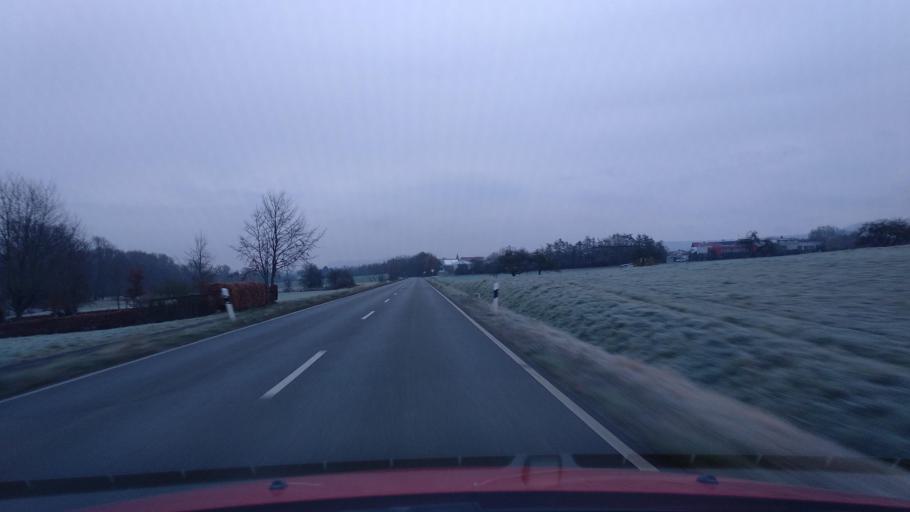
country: DE
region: Hesse
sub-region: Regierungsbezirk Kassel
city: Calden
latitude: 51.3747
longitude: 9.3831
